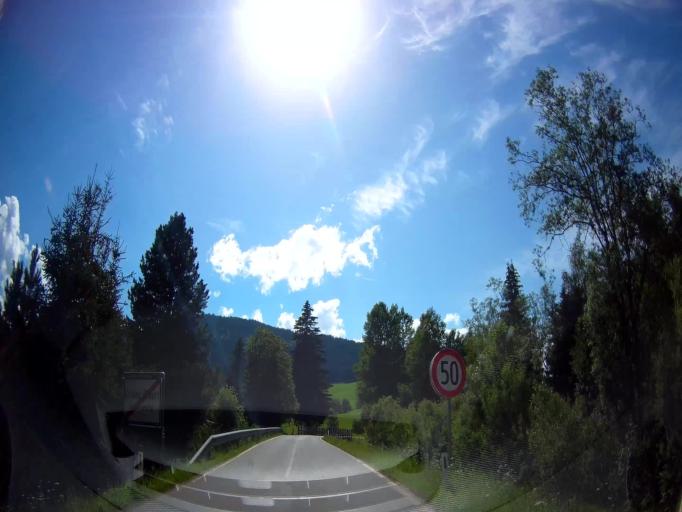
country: AT
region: Salzburg
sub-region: Politischer Bezirk Tamsweg
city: Thomatal
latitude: 47.0790
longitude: 13.7338
